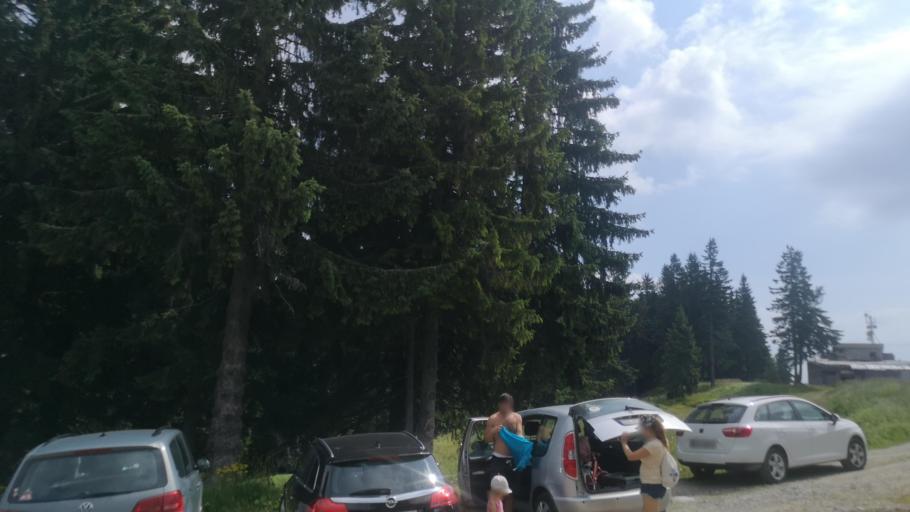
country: SK
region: Zilinsky
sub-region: Okres Zilina
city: Vrutky
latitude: 49.0927
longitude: 18.8348
